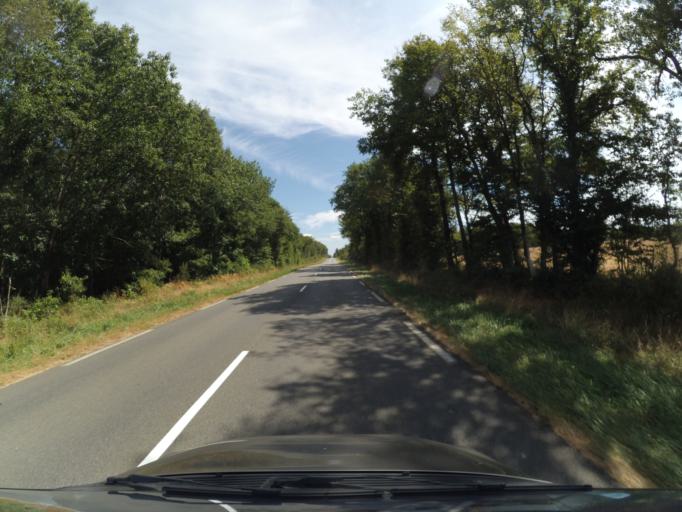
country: FR
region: Poitou-Charentes
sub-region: Departement de la Vienne
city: Availles-Limouzine
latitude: 46.0631
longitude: 0.6028
